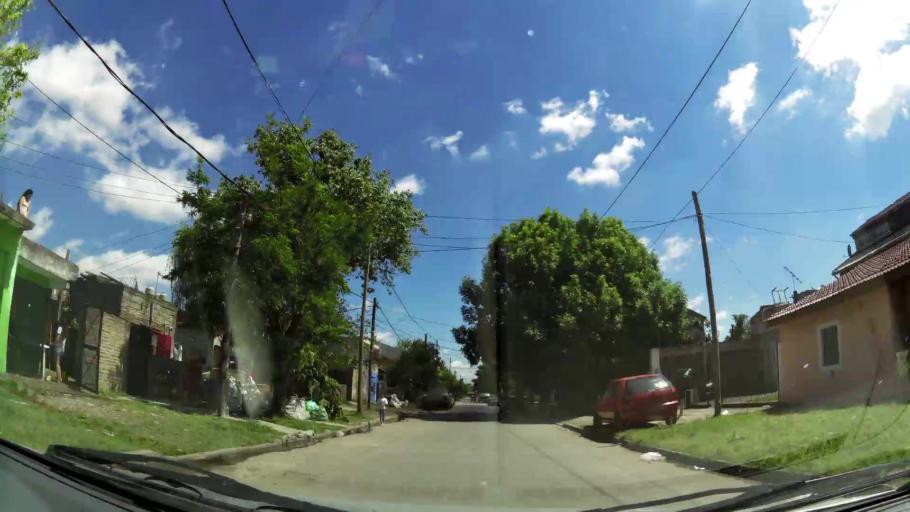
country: AR
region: Buenos Aires
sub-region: Partido de Lanus
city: Lanus
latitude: -34.6950
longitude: -58.4304
